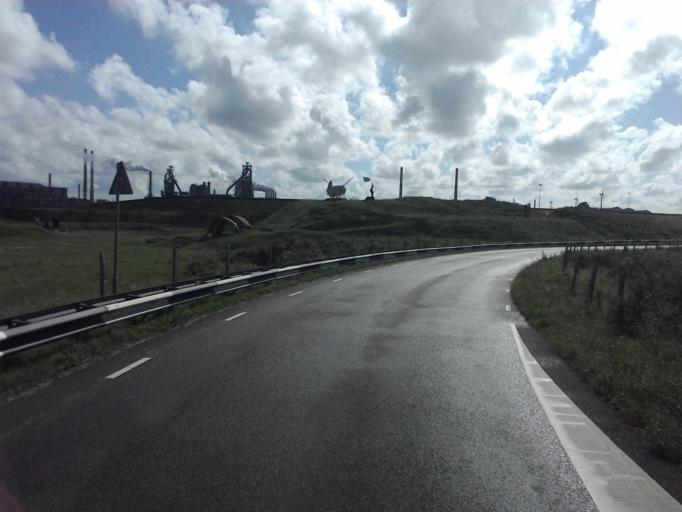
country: NL
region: North Holland
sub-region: Gemeente Velsen
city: Velsen-Zuid
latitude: 52.4888
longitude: 4.5914
